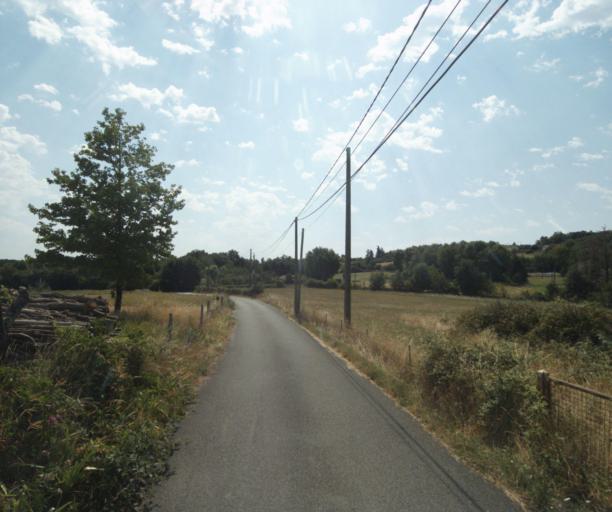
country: FR
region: Rhone-Alpes
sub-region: Departement du Rhone
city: Lentilly
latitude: 45.8503
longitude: 4.6521
